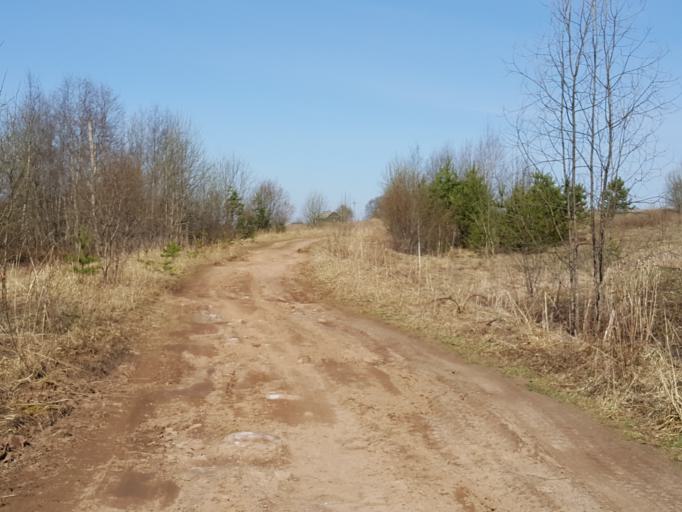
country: RU
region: Leningrad
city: Podporozh'ye
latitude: 60.3541
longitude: 34.8410
